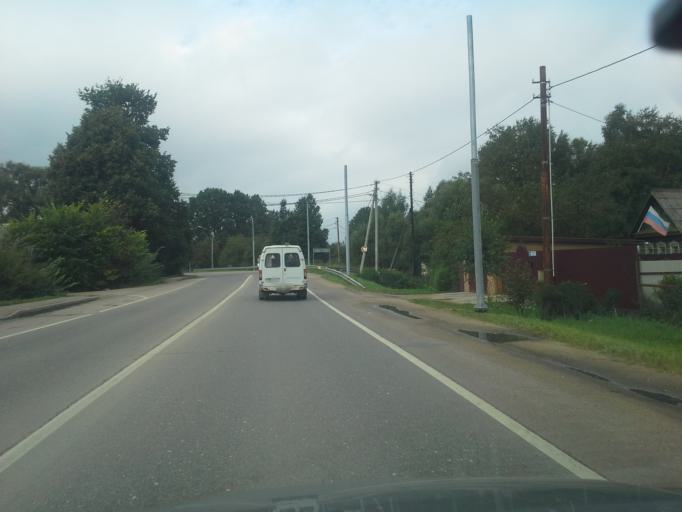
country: RU
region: Moskovskaya
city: Chupryakovo
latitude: 55.5732
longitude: 36.6601
